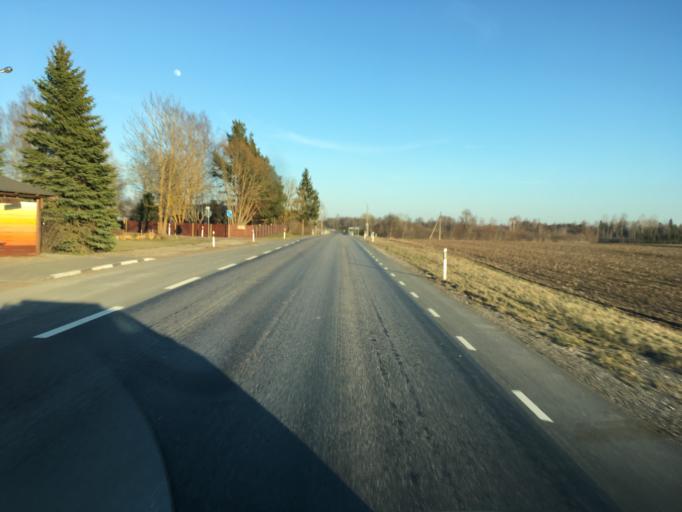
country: EE
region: Raplamaa
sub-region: Rapla vald
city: Rapla
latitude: 59.0822
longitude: 24.8252
